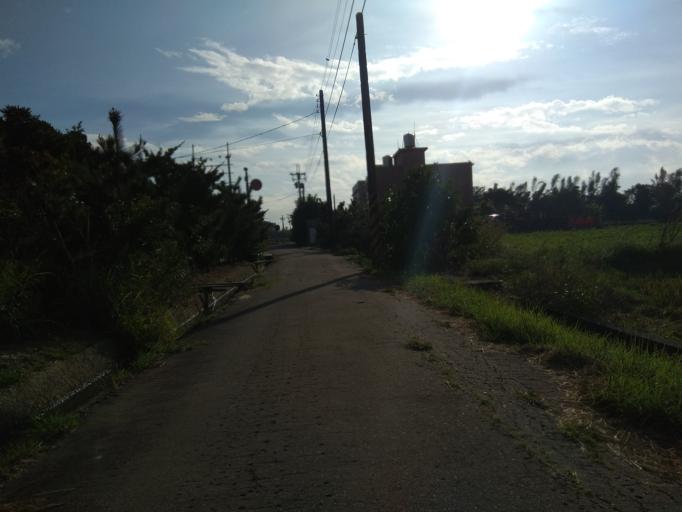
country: TW
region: Taiwan
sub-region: Hsinchu
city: Zhubei
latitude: 24.9782
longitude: 121.0606
